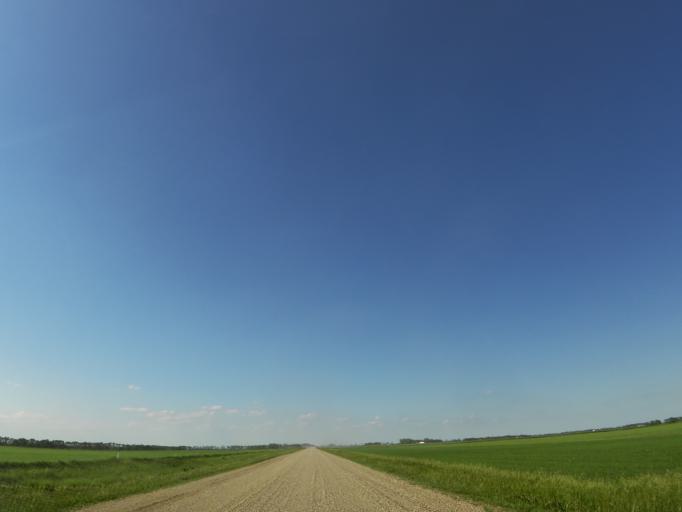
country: US
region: North Dakota
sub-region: Walsh County
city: Grafton
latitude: 48.3342
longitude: -97.2552
